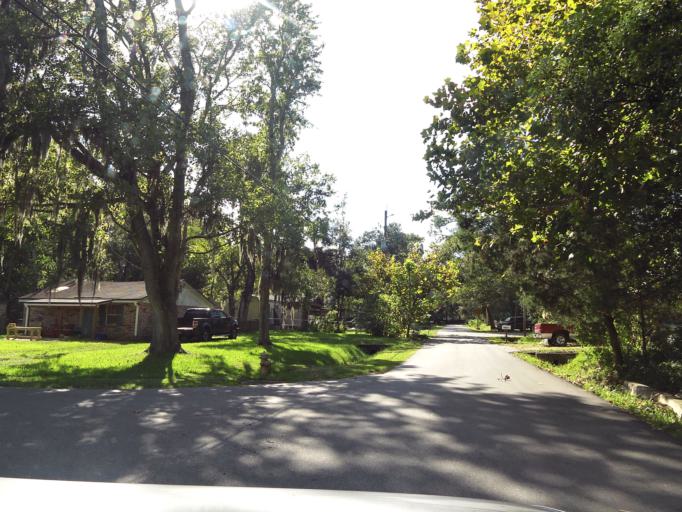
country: US
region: Florida
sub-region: Duval County
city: Jacksonville
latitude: 30.2743
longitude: -81.6333
